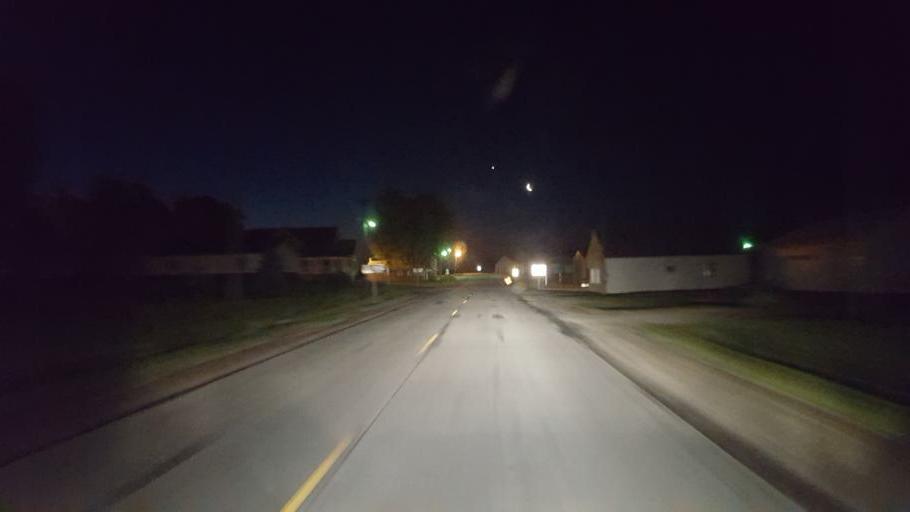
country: US
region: Iowa
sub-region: Decatur County
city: Lamoni
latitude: 40.4756
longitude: -93.9279
